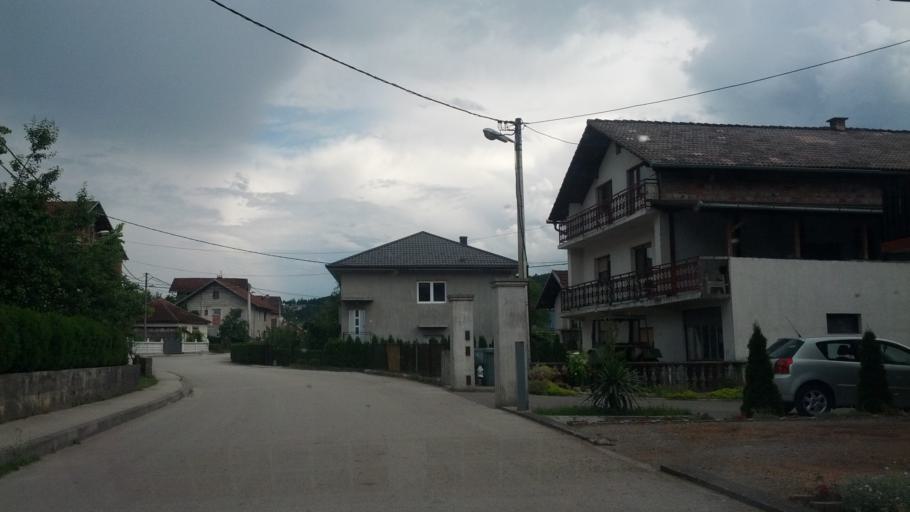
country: BA
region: Federation of Bosnia and Herzegovina
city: Bosanska Krupa
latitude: 44.8886
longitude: 16.1385
